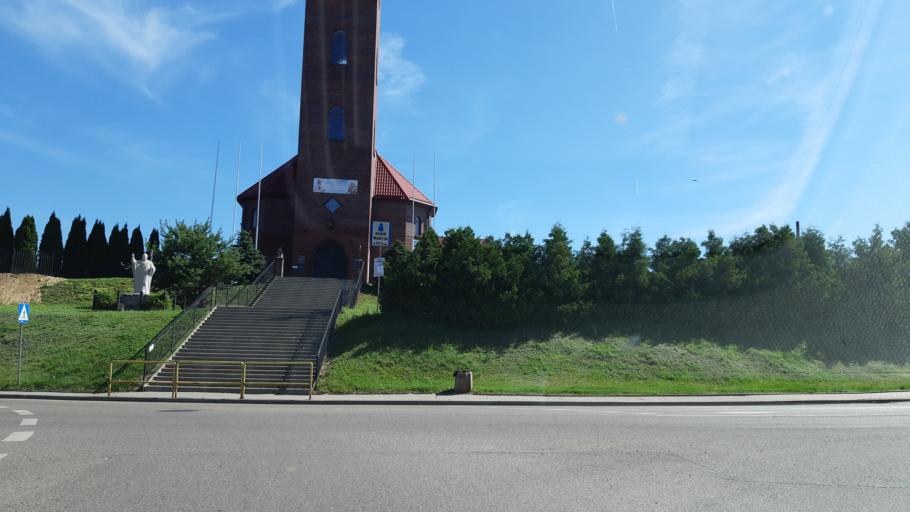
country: PL
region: Warmian-Masurian Voivodeship
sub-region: Powiat mragowski
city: Mikolajki
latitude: 53.8008
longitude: 21.5759
